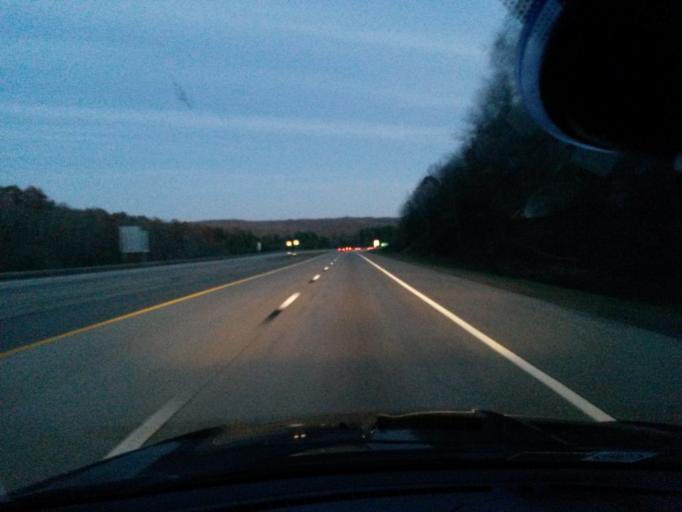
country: US
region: West Virginia
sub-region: Raleigh County
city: Daniels
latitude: 37.7730
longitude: -81.0547
